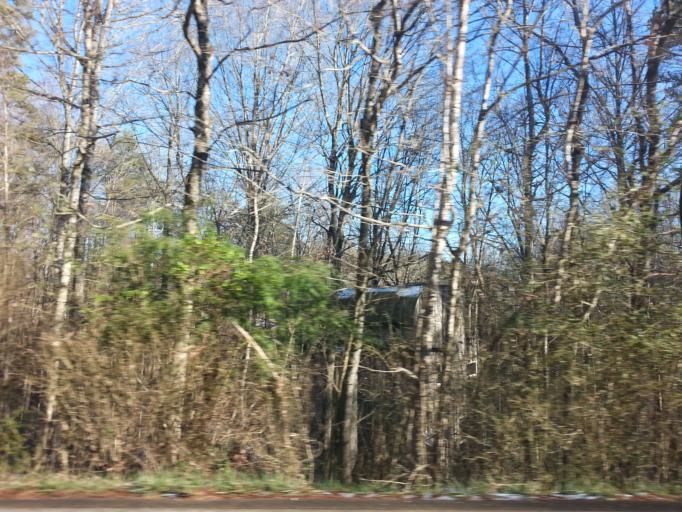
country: US
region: Tennessee
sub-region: Blount County
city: Louisville
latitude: 35.9006
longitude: -84.0026
